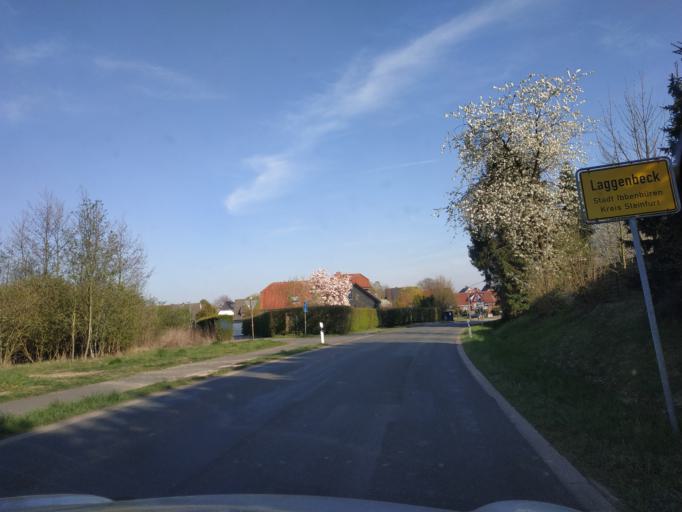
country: DE
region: North Rhine-Westphalia
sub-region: Regierungsbezirk Munster
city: Mettingen
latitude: 52.2708
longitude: 7.7867
